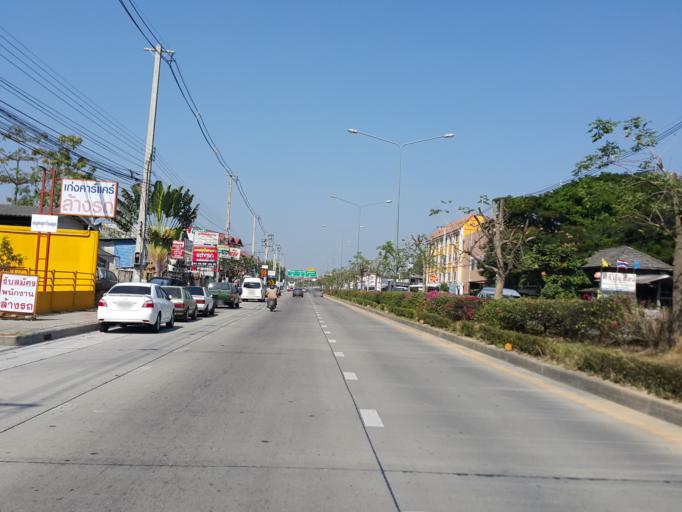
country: TH
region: Chiang Mai
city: San Sai
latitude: 18.8025
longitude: 99.0311
